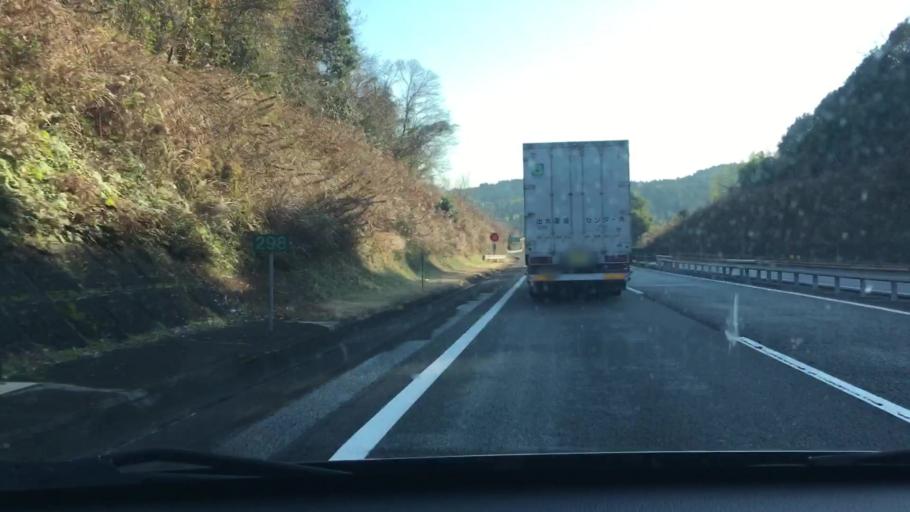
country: JP
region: Kagoshima
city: Kajiki
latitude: 31.8832
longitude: 130.6955
